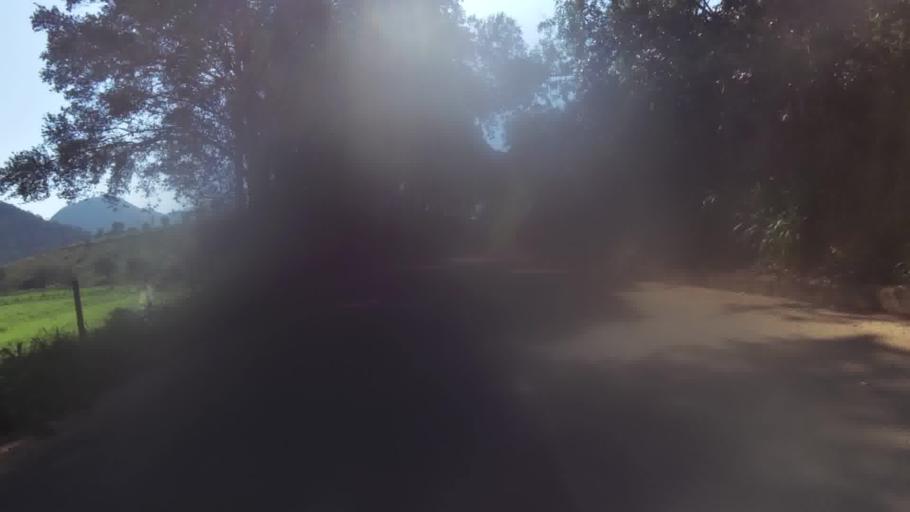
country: BR
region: Espirito Santo
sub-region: Alfredo Chaves
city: Alfredo Chaves
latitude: -20.6556
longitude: -40.7603
